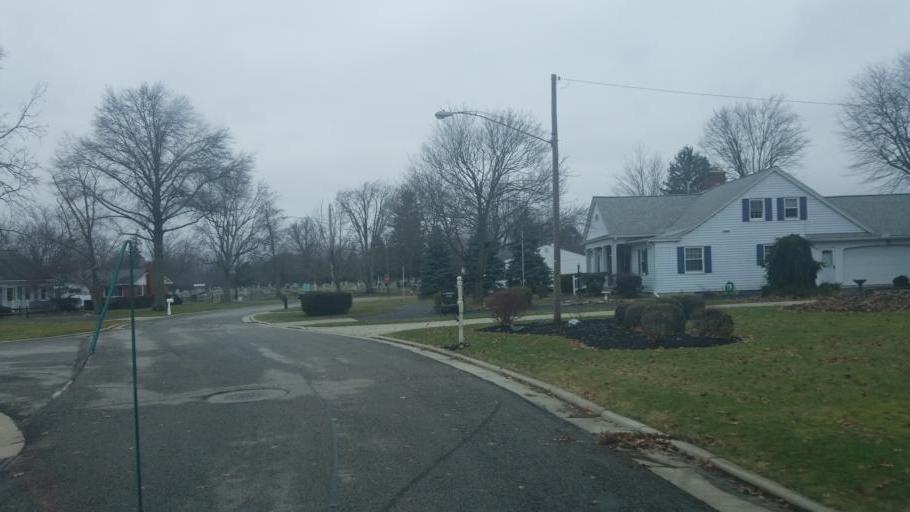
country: US
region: Ohio
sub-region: Crawford County
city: Bucyrus
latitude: 40.7964
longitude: -82.9845
